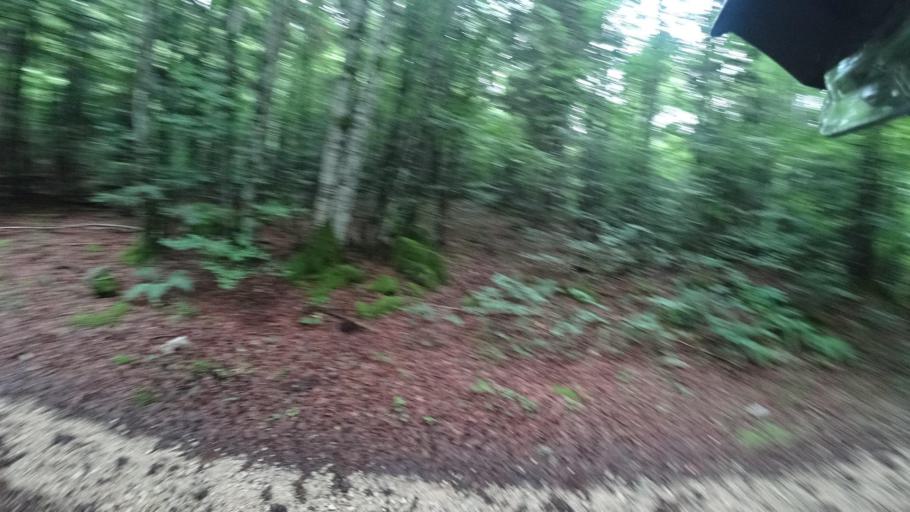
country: HR
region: Licko-Senjska
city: Jezerce
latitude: 44.7921
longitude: 15.6378
